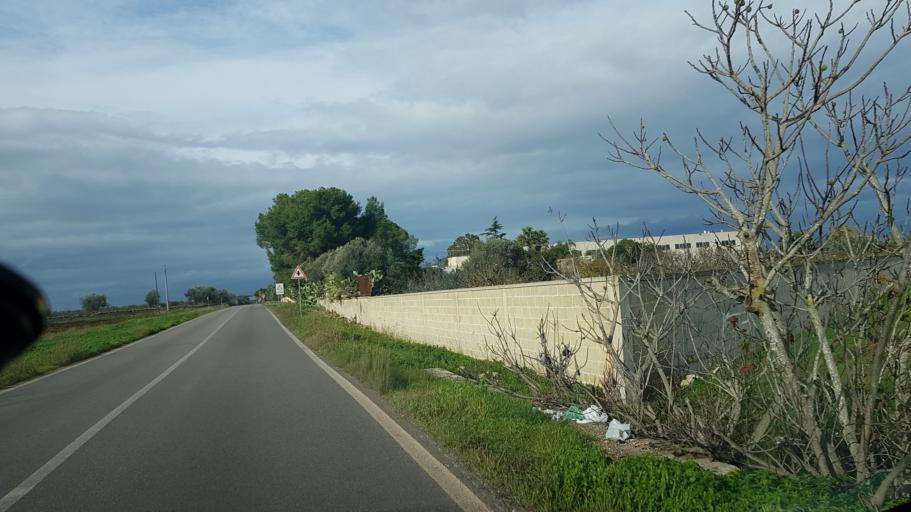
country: IT
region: Apulia
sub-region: Provincia di Brindisi
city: Torre Santa Susanna
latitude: 40.4801
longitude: 17.6896
